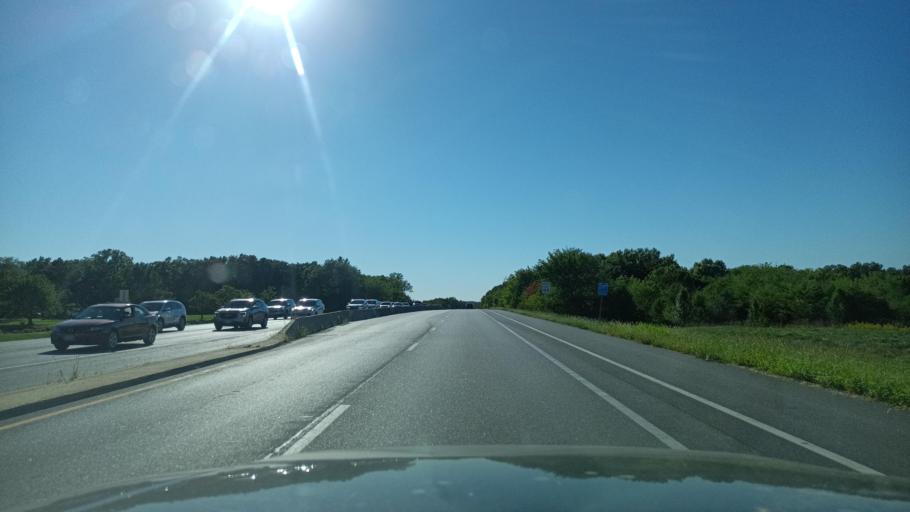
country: US
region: Missouri
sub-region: Boone County
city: Columbia
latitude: 38.9316
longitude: -92.2987
